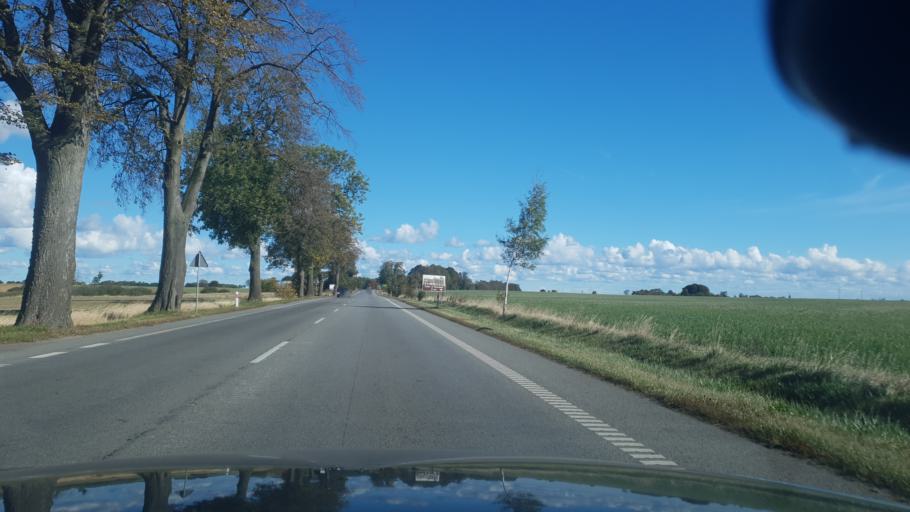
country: PL
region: Pomeranian Voivodeship
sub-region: Powiat wejherowski
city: Rekowo Dolne
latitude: 54.6669
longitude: 18.3679
